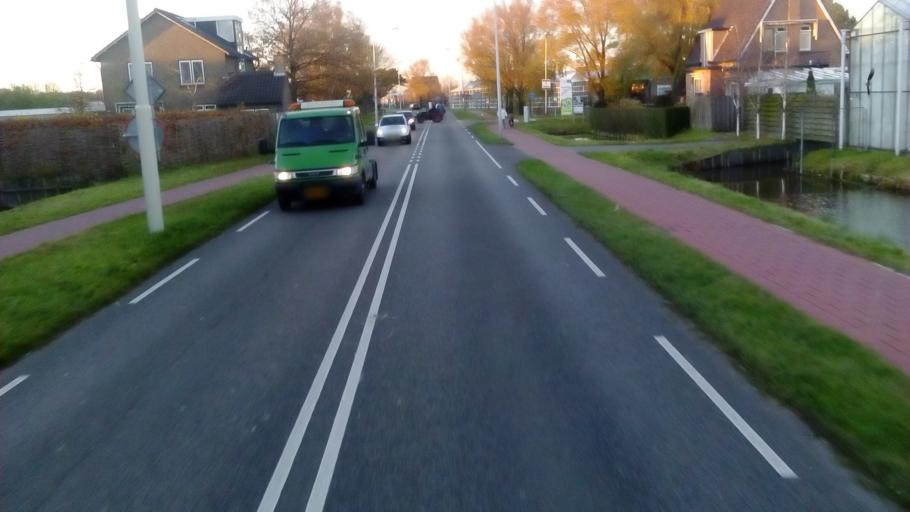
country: NL
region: South Holland
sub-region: Gemeente Westland
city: Naaldwijk
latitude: 52.0042
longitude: 4.2054
